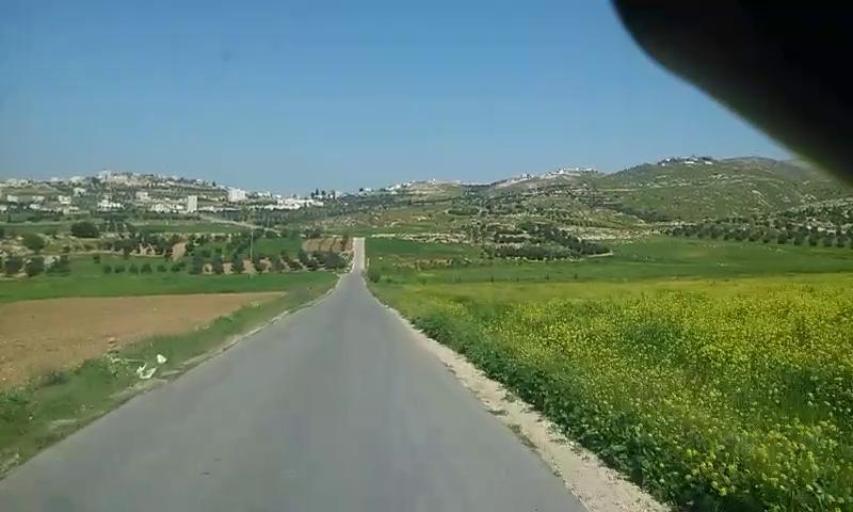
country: PS
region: West Bank
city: Al Majd
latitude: 31.4931
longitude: 34.9590
